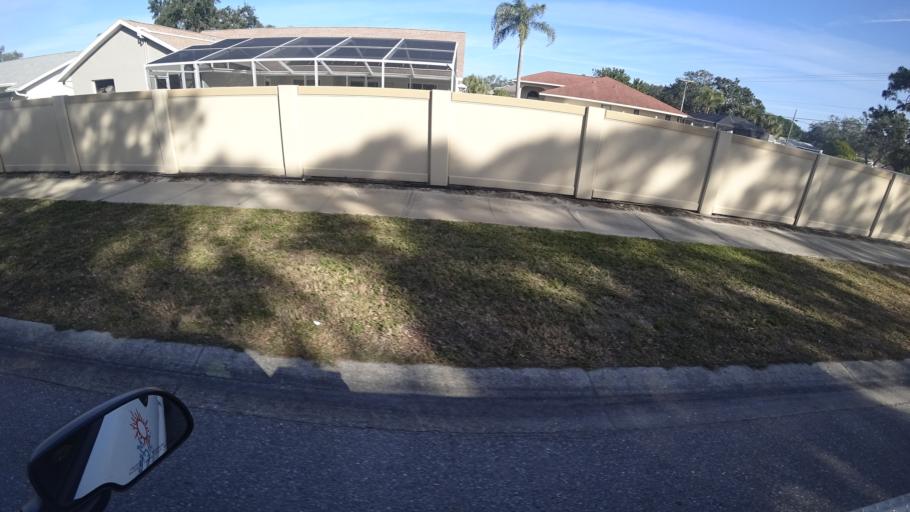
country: US
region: Florida
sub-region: Manatee County
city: West Bradenton
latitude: 27.4812
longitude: -82.6126
